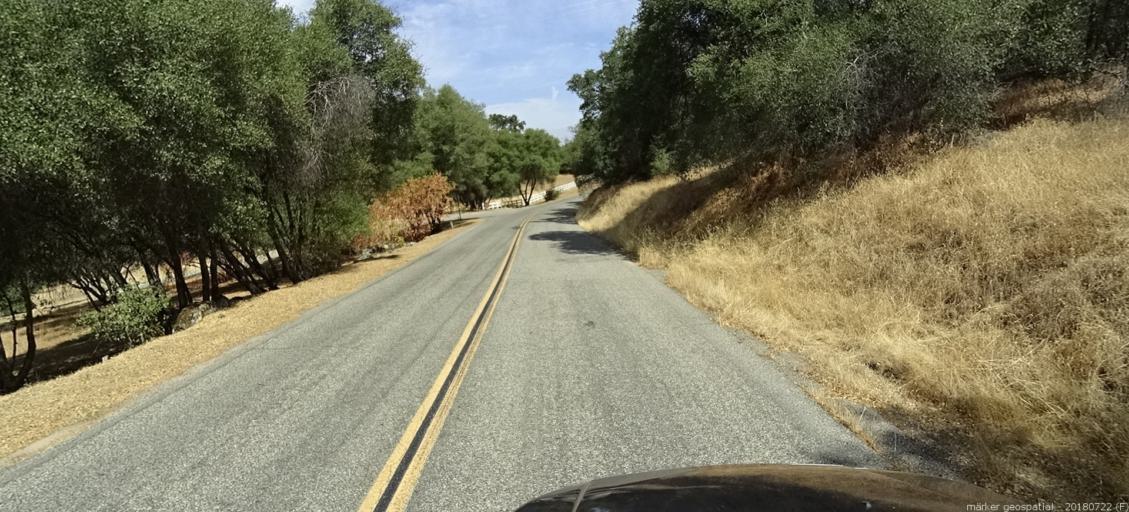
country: US
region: California
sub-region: Madera County
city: Coarsegold
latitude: 37.2532
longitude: -119.7332
